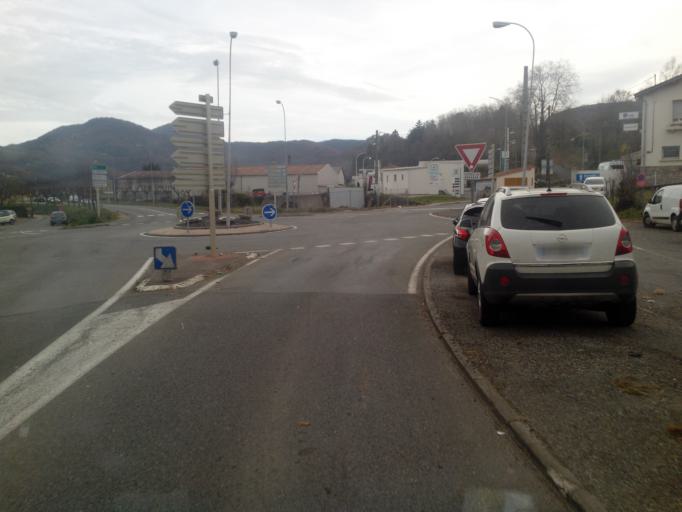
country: FR
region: Midi-Pyrenees
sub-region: Departement de l'Ariege
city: Saint-Girons
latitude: 42.9805
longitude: 1.1436
